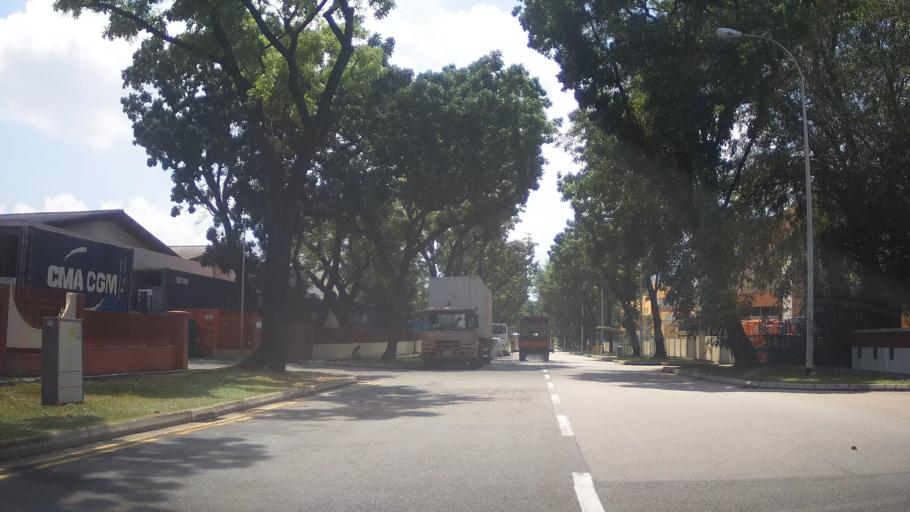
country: MY
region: Johor
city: Johor Bahru
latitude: 1.3313
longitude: 103.7099
